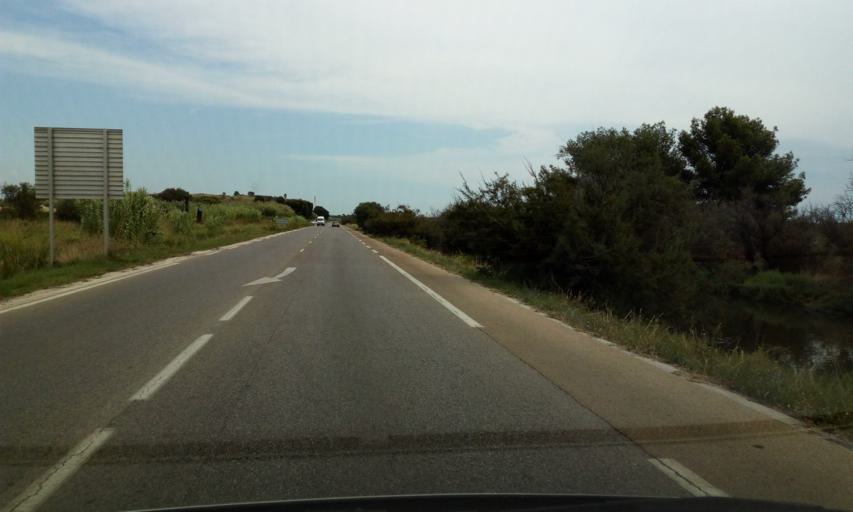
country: FR
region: Provence-Alpes-Cote d'Azur
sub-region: Departement du Var
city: Hyeres
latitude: 43.0802
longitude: 6.1296
